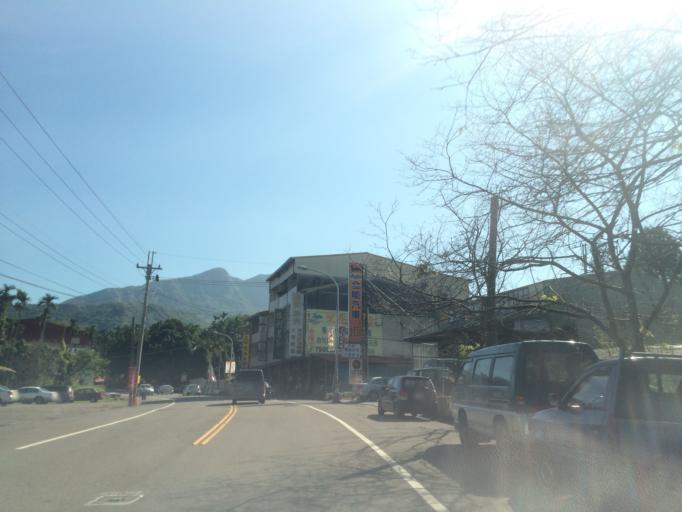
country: TW
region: Taiwan
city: Lugu
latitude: 23.7351
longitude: 120.7625
